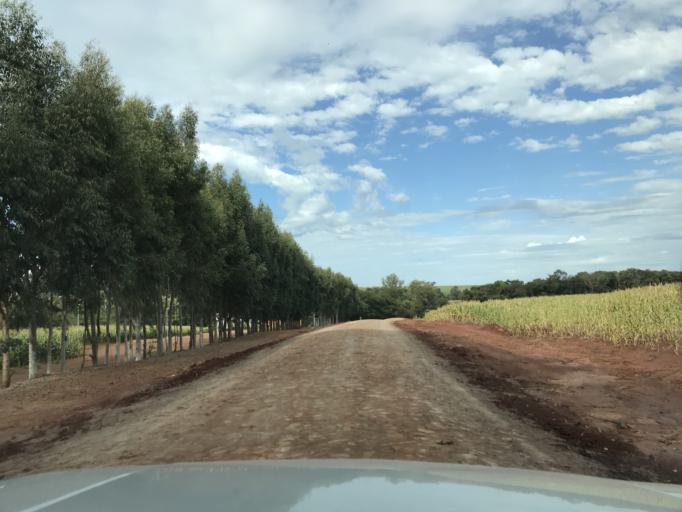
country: BR
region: Parana
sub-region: Palotina
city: Palotina
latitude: -24.2997
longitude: -53.8117
